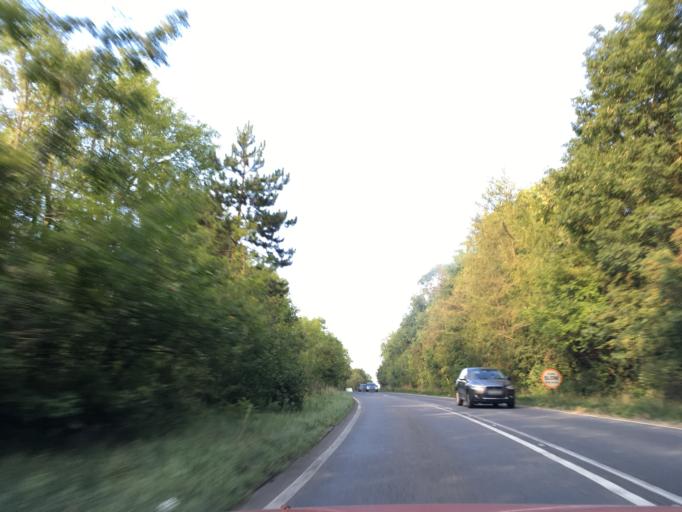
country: GB
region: England
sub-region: Gloucestershire
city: Bourton on the Water
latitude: 51.8686
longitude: -1.7928
